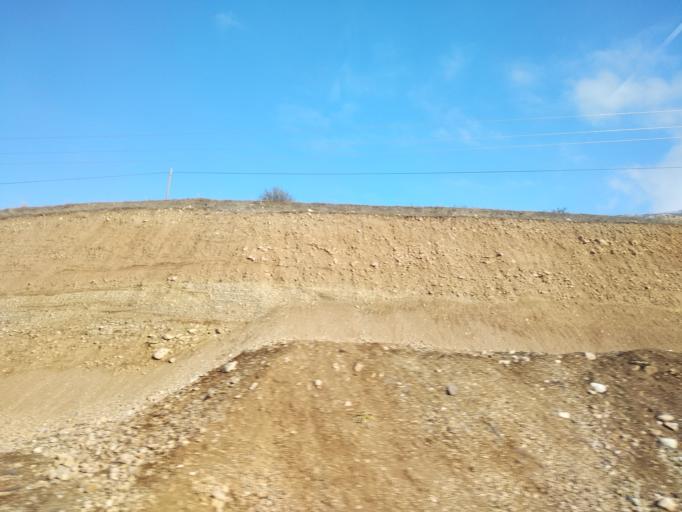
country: TR
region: Gumushane
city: Kelkit
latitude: 40.0130
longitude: 39.5300
